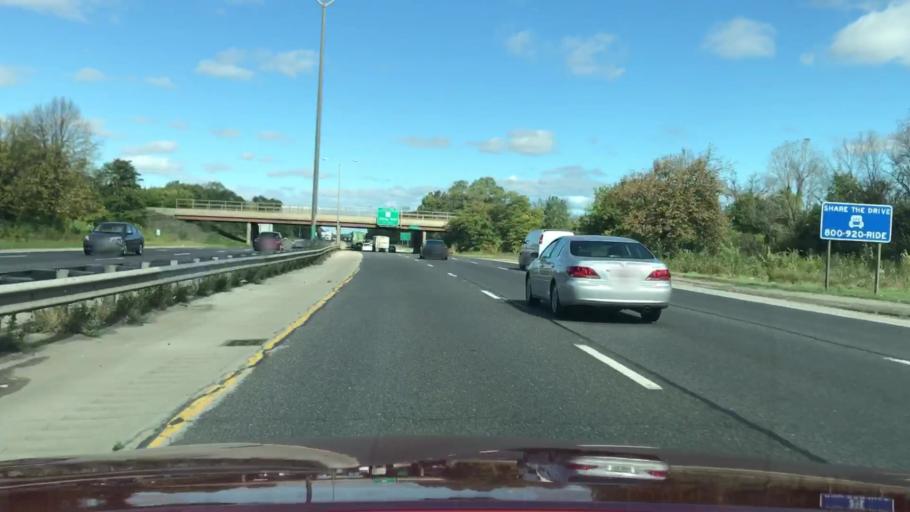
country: US
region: Illinois
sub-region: Cook County
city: South Holland
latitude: 41.6138
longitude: -87.5789
